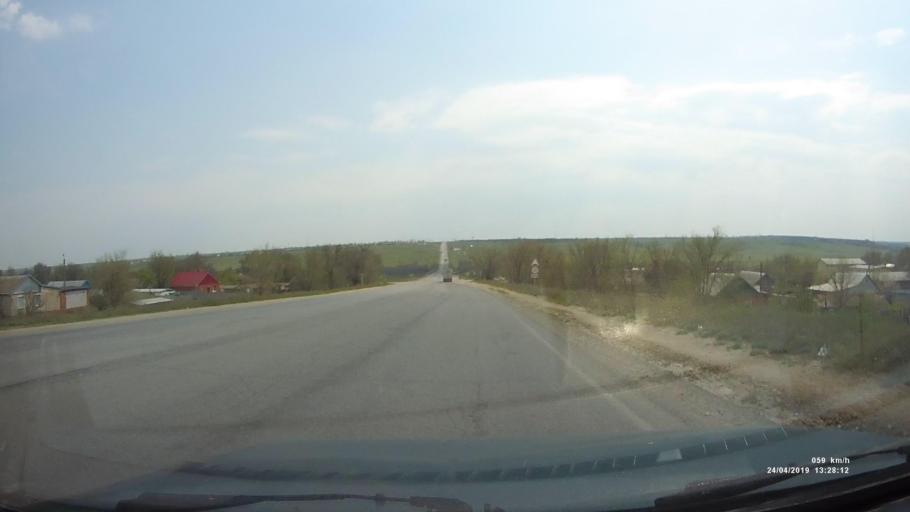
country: RU
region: Kalmykiya
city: Arshan'
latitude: 46.2749
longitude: 44.2285
